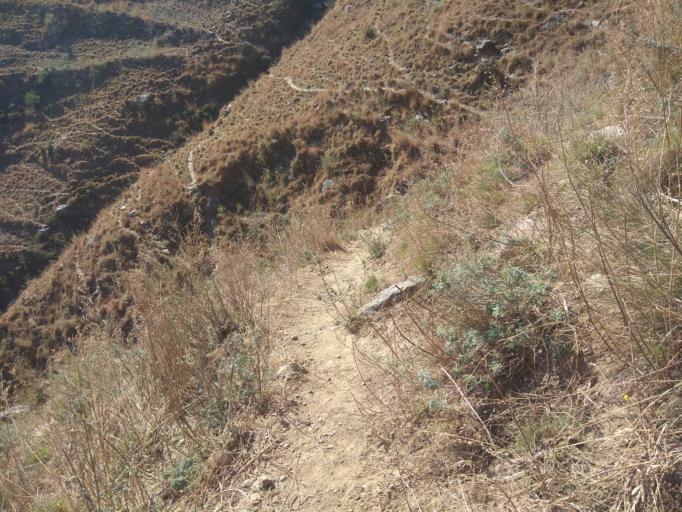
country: NP
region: Mid Western
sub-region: Karnali Zone
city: Jumla
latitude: 29.3158
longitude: 81.7424
